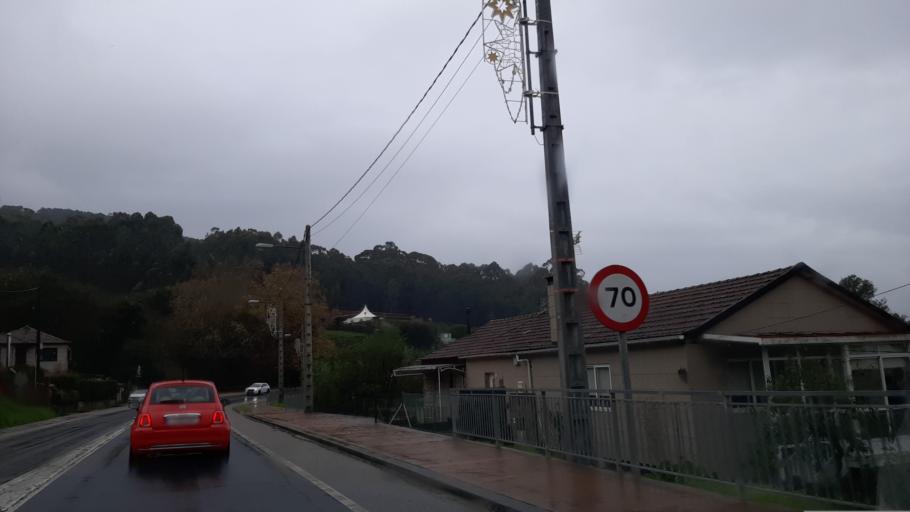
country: ES
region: Galicia
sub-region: Provincia de Pontevedra
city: Nigran
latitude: 42.1843
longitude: -8.7879
